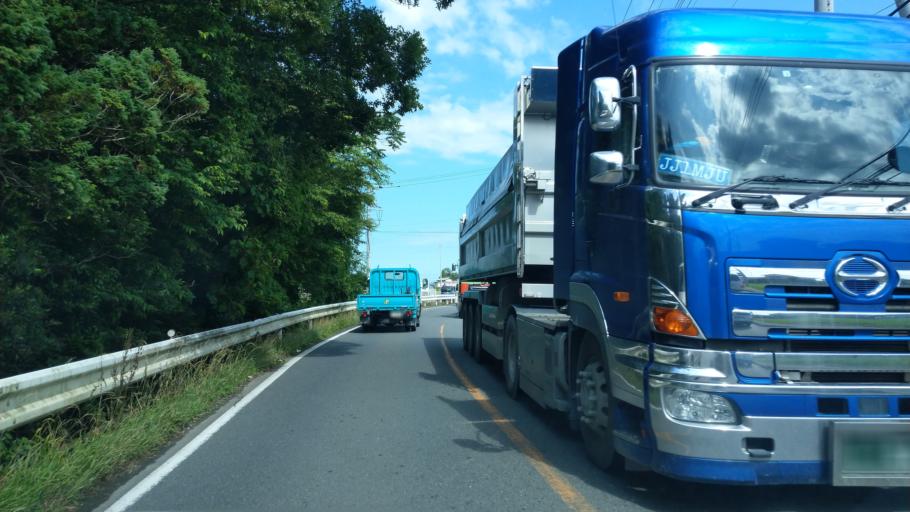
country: JP
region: Saitama
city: Okegawa
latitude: 35.9621
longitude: 139.5119
